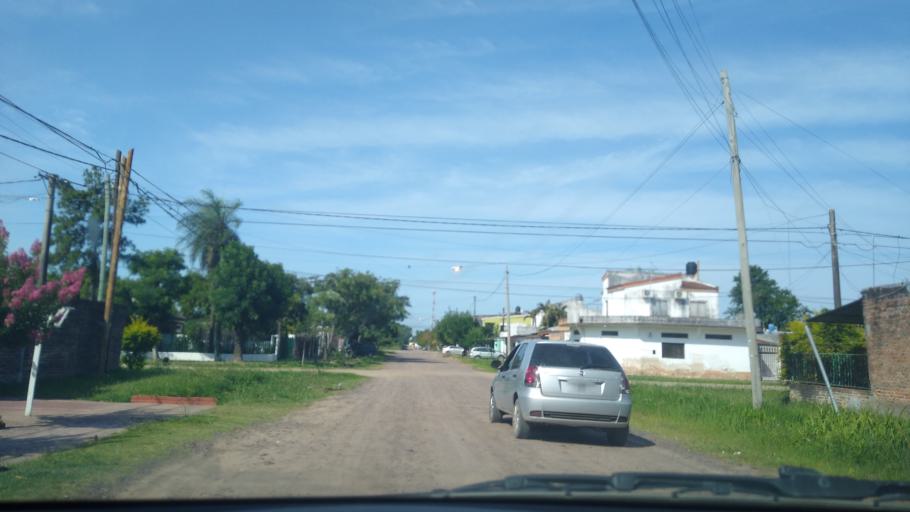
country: AR
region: Chaco
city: Barranqueras
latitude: -27.4881
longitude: -58.9471
